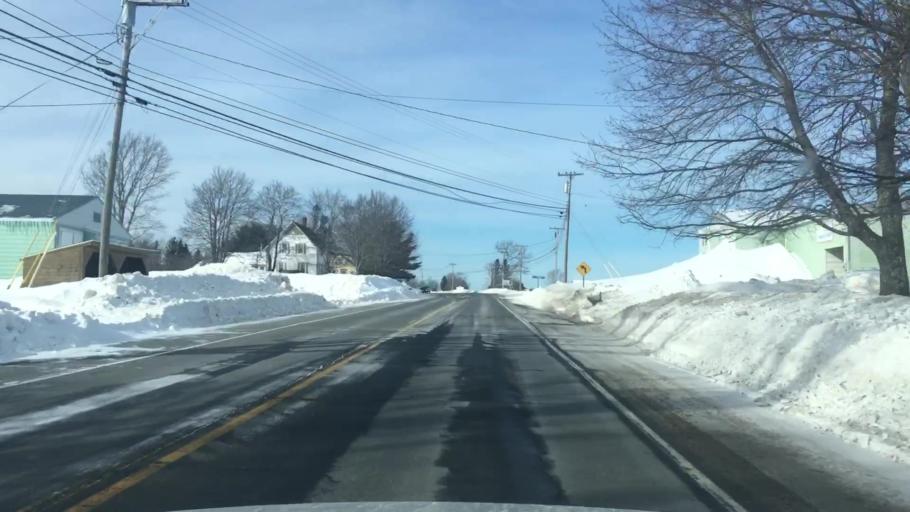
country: US
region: Maine
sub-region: Penobscot County
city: Charleston
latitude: 45.0257
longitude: -69.0301
